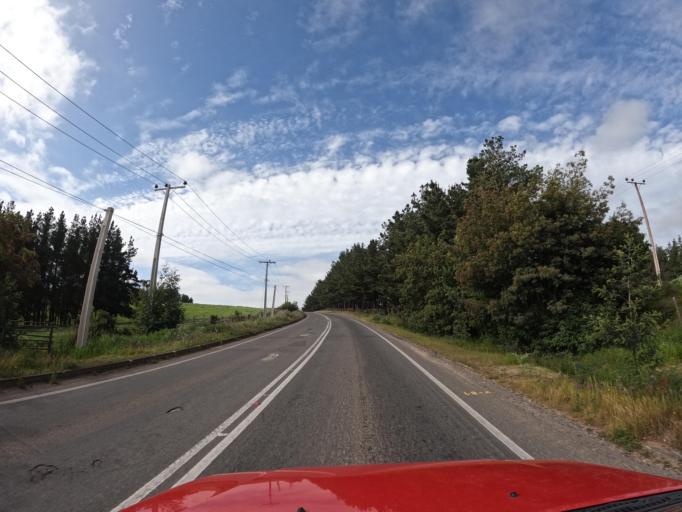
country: CL
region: O'Higgins
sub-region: Provincia de Colchagua
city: Santa Cruz
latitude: -34.3582
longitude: -71.9445
